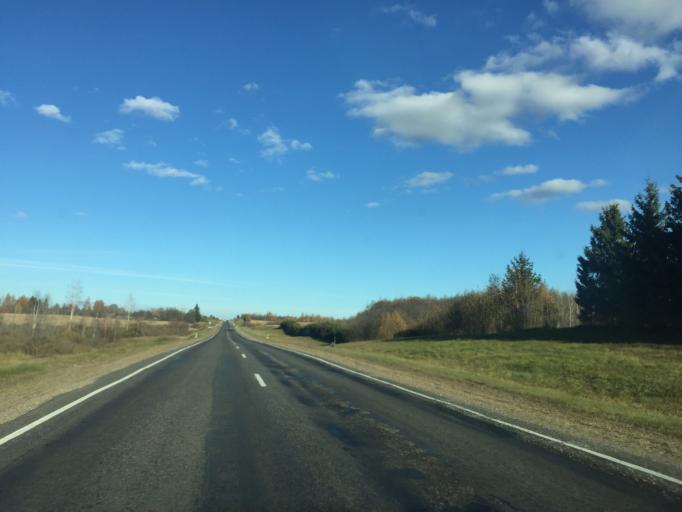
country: BY
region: Vitebsk
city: Dzisna
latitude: 55.2796
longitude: 28.1665
